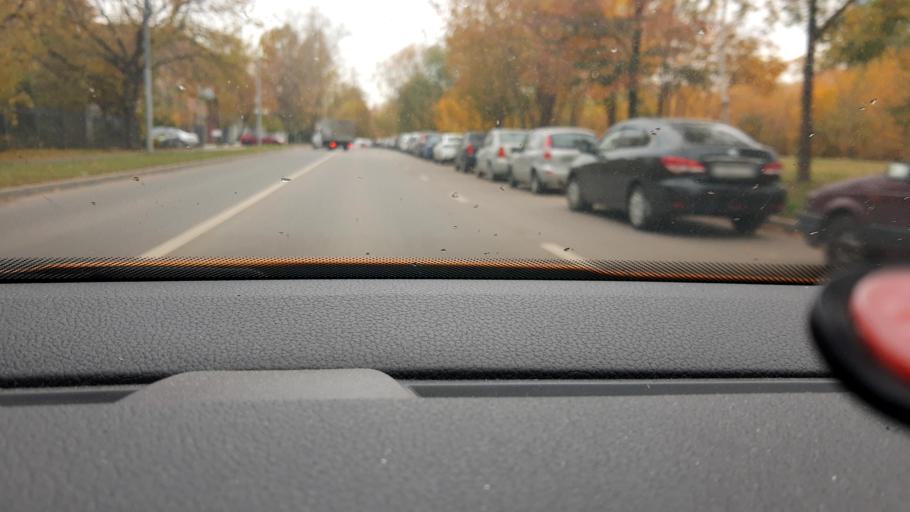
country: RU
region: Moscow
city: Zapadnoye Degunino
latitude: 55.8525
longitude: 37.5386
